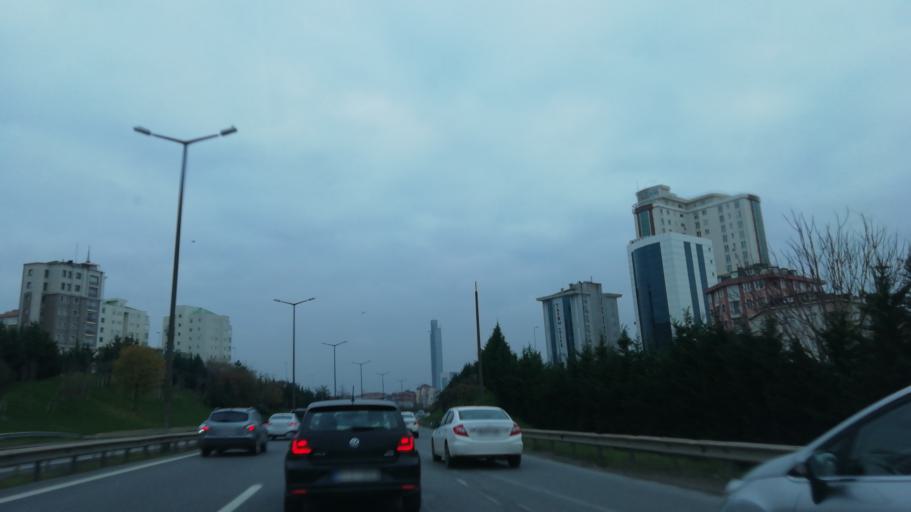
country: TR
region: Istanbul
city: Umraniye
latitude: 41.0093
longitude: 29.0905
